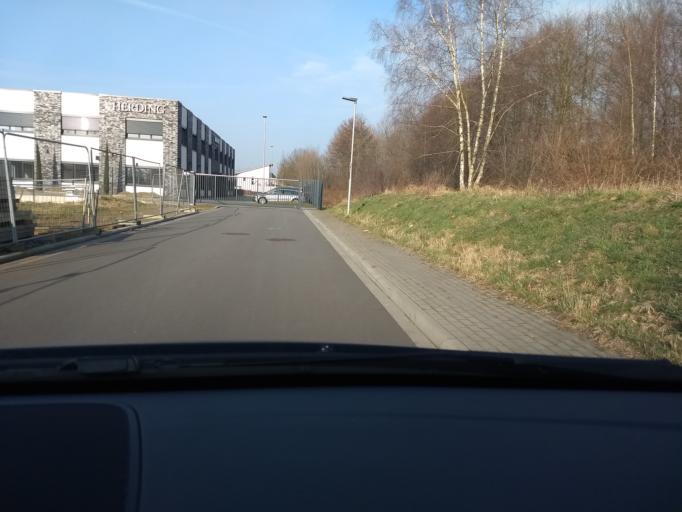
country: DE
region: North Rhine-Westphalia
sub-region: Regierungsbezirk Munster
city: Rhede
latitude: 51.8355
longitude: 6.7198
